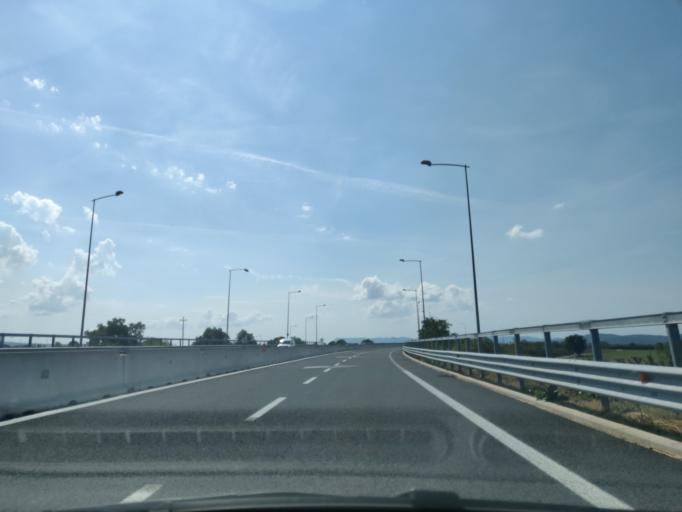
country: IT
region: Latium
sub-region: Provincia di Viterbo
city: Blera
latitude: 42.3102
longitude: 11.9920
